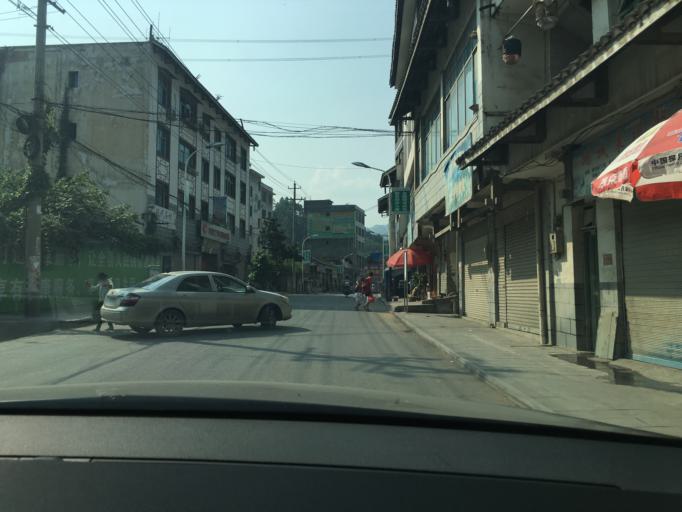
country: CN
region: Guangxi Zhuangzu Zizhiqu
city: Xinzhou
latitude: 24.9879
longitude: 105.8012
